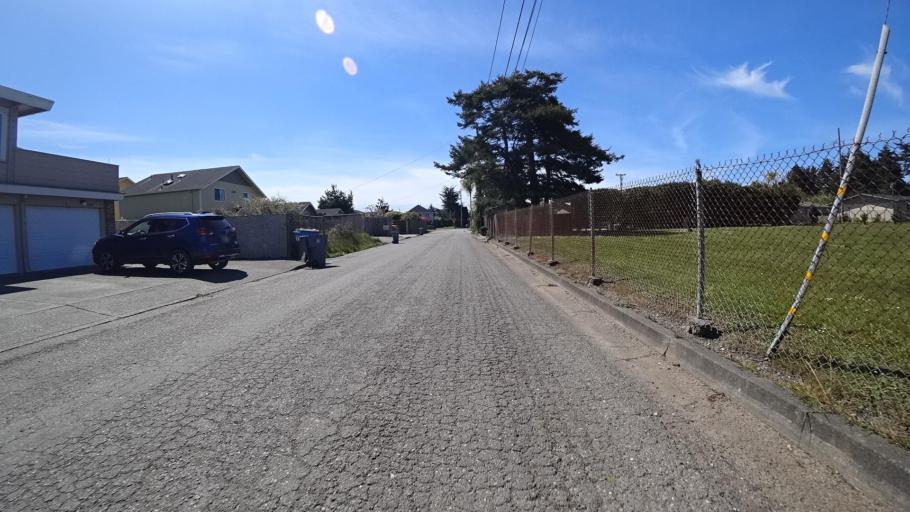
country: US
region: California
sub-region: Humboldt County
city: Eureka
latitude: 40.7985
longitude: -124.1491
